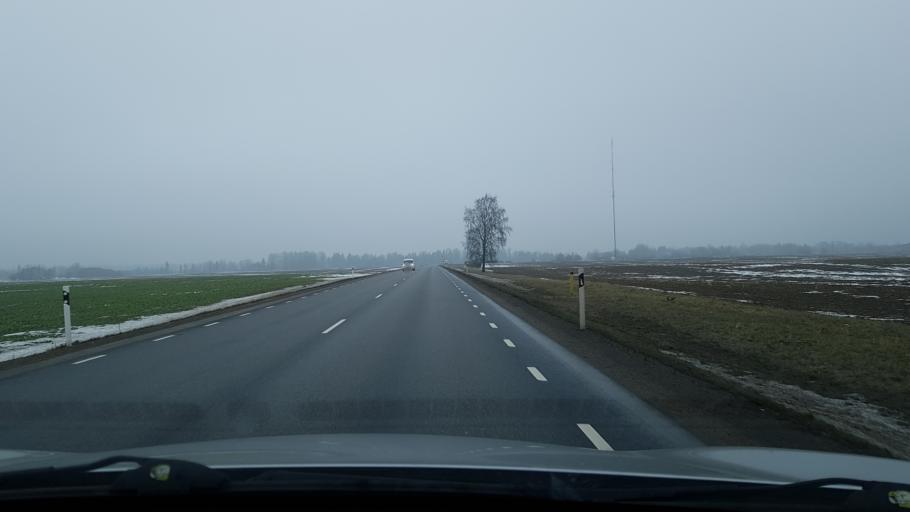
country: EE
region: Viljandimaa
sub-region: Viiratsi vald
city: Viiratsi
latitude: 58.3479
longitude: 25.6263
